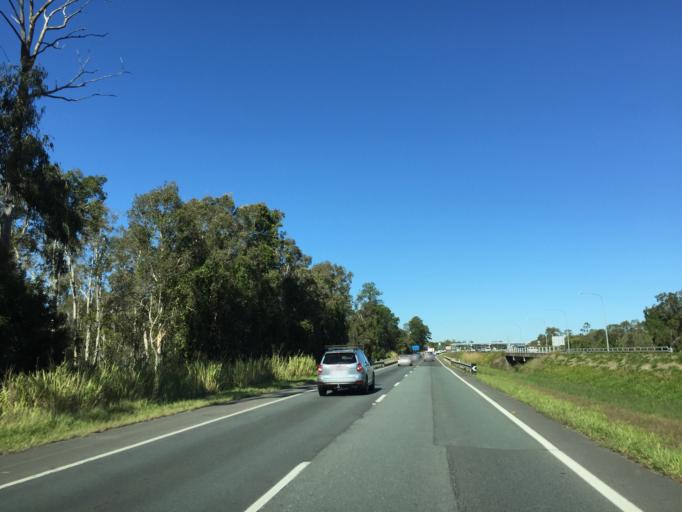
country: AU
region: Queensland
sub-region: Moreton Bay
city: Caboolture
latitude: -27.0639
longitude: 152.9776
